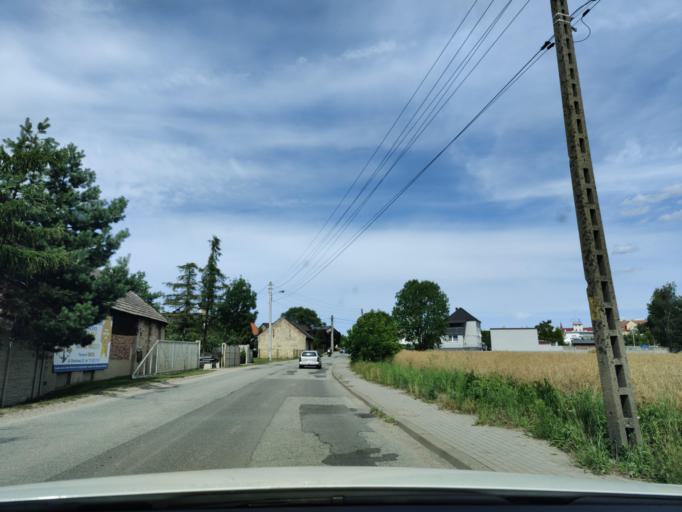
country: PL
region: Opole Voivodeship
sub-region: Powiat krapkowicki
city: Strzeleczki
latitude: 50.4567
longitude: 17.8504
